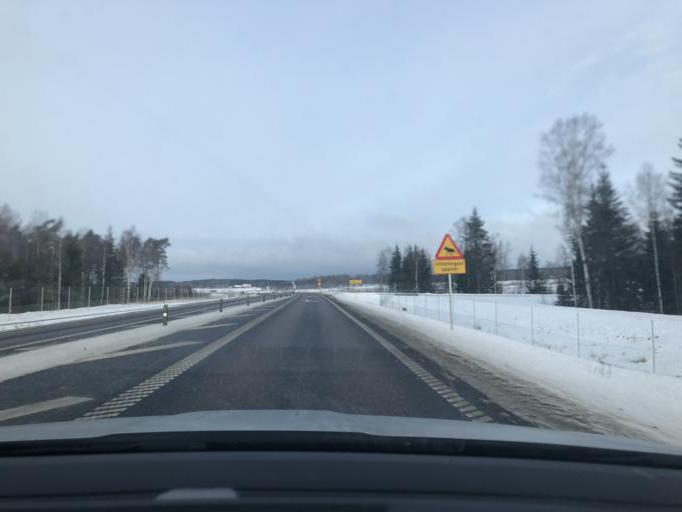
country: SE
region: OEstergoetland
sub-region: Motala Kommun
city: Borensberg
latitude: 58.5737
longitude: 15.2392
